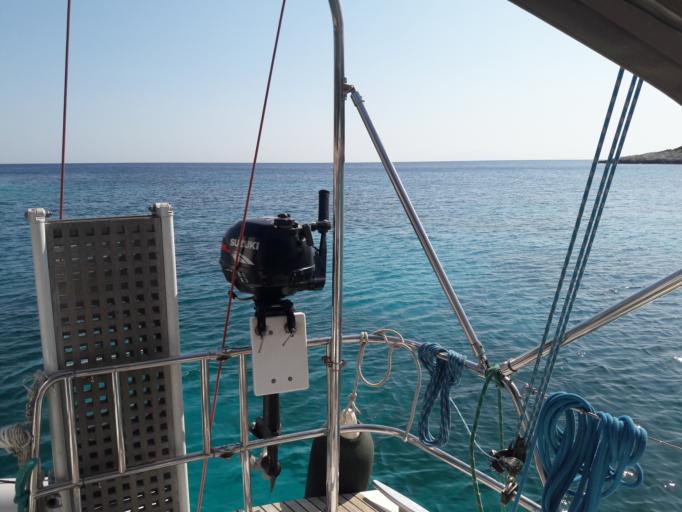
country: GR
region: Central Greece
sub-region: Nomos Evvoias
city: Skyros
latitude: 38.8340
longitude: 24.3675
